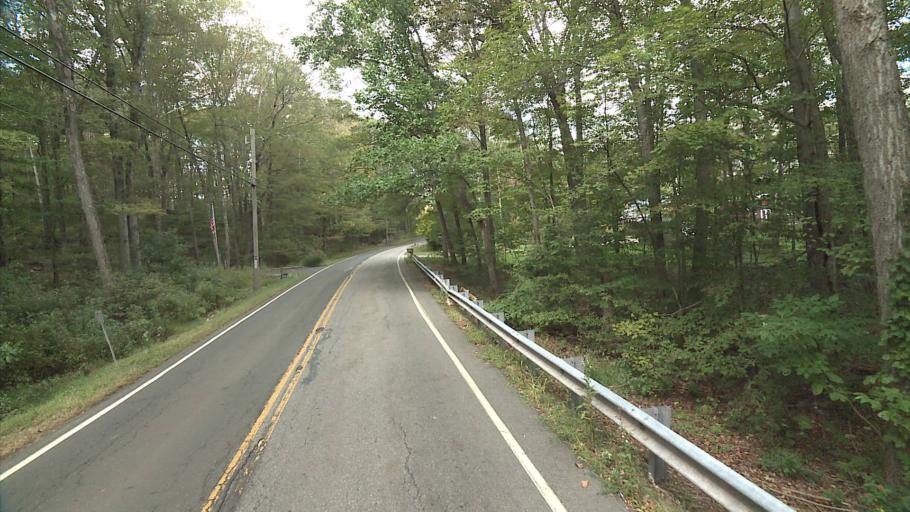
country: US
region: Connecticut
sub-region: Middlesex County
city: Higganum
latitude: 41.4053
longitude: -72.6060
